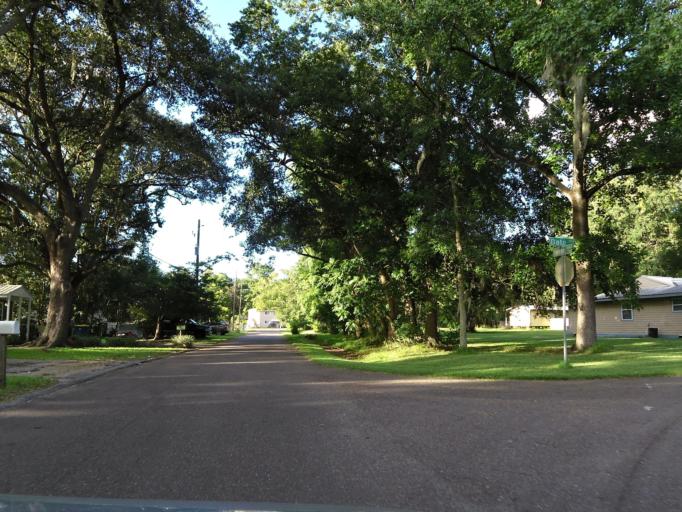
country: US
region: Florida
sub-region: Duval County
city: Jacksonville
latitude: 30.4230
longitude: -81.6982
